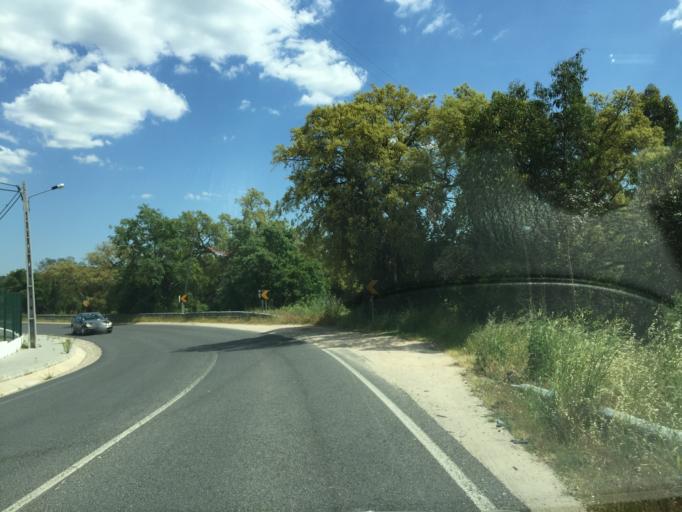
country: PT
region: Santarem
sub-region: Ourem
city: Ourem
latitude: 39.6544
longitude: -8.5951
